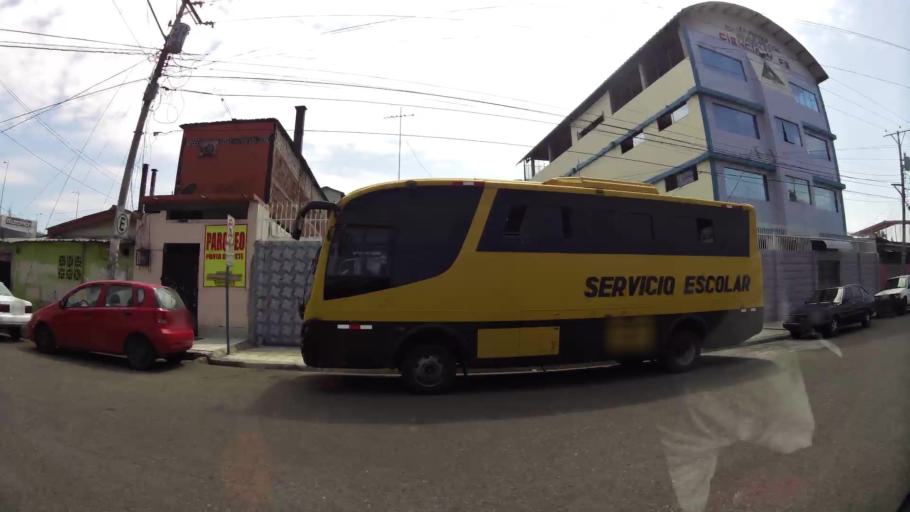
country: EC
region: Guayas
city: Guayaquil
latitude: -2.2312
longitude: -79.8969
